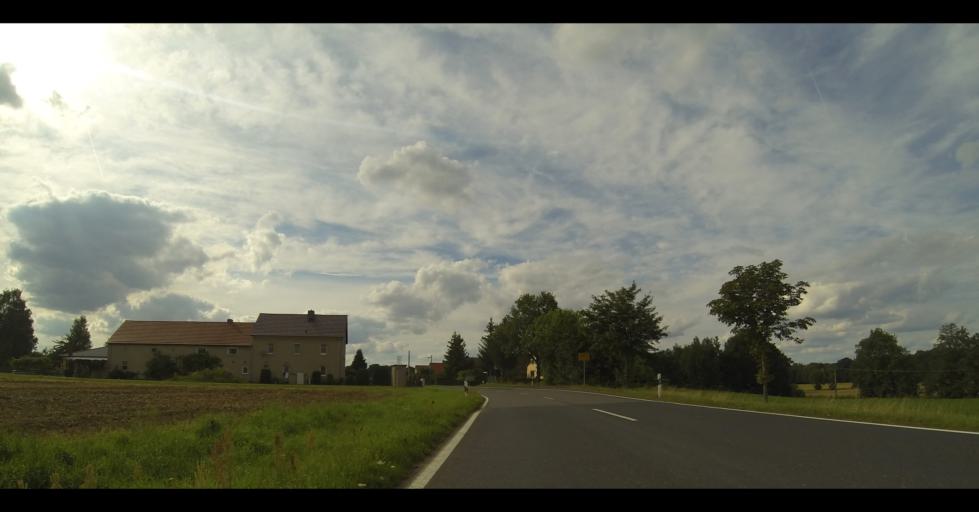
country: DE
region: Saxony
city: Radeburg
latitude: 51.2248
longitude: 13.7077
